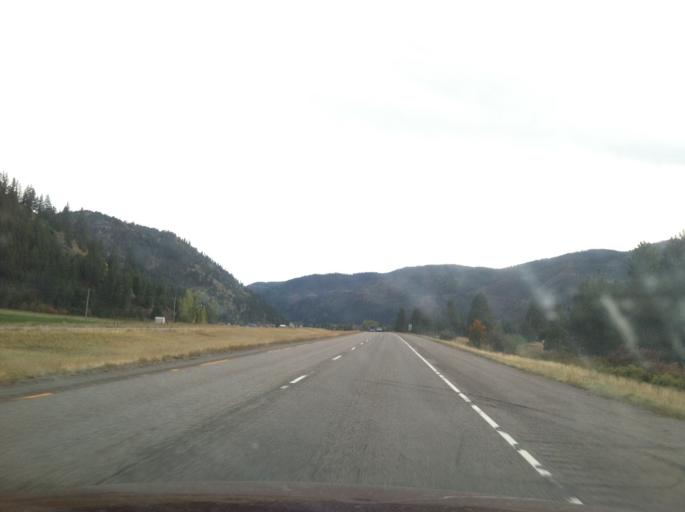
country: US
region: Montana
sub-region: Missoula County
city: Clinton
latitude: 46.7714
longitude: -113.7111
